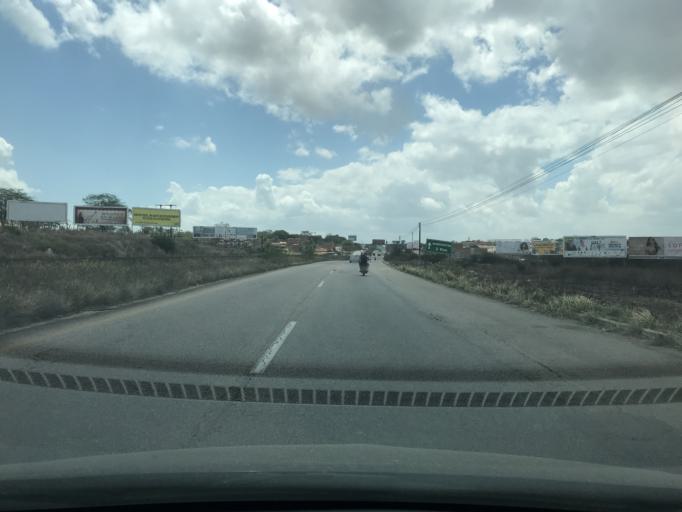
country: BR
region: Pernambuco
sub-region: Caruaru
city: Caruaru
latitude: -8.3086
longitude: -35.9525
